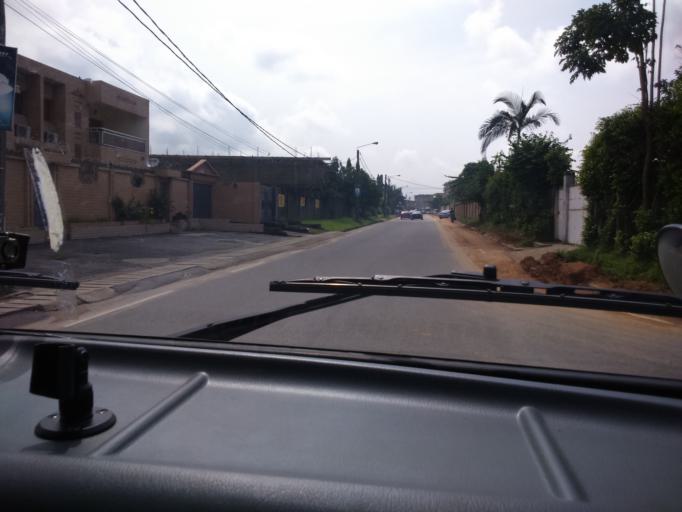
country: CI
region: Lagunes
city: Abidjan
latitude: 5.3556
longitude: -3.9804
